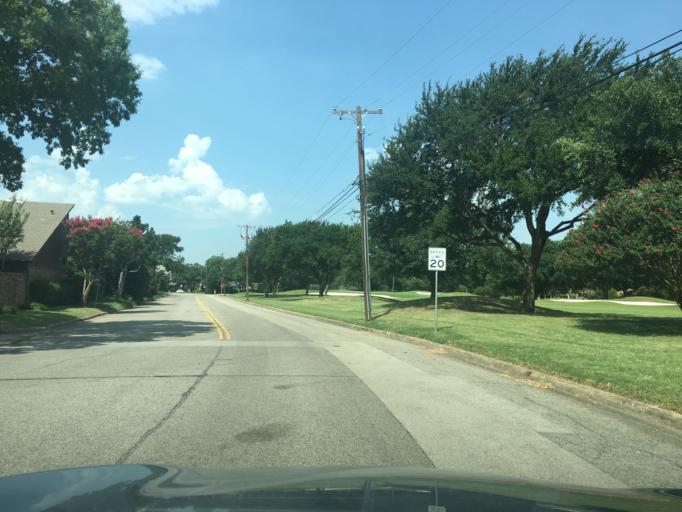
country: US
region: Texas
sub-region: Dallas County
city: Farmers Branch
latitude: 32.9328
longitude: -96.8630
